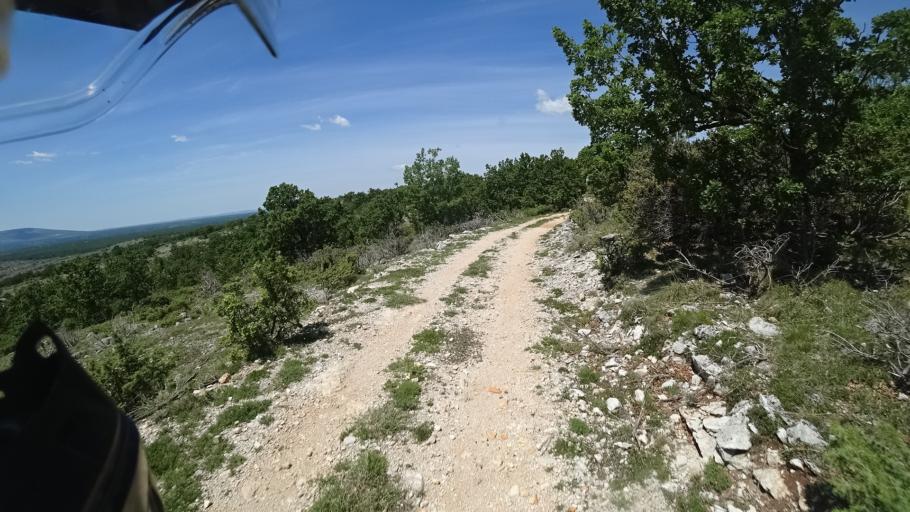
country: HR
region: Sibensko-Kniniska
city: Knin
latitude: 44.0298
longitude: 16.2861
